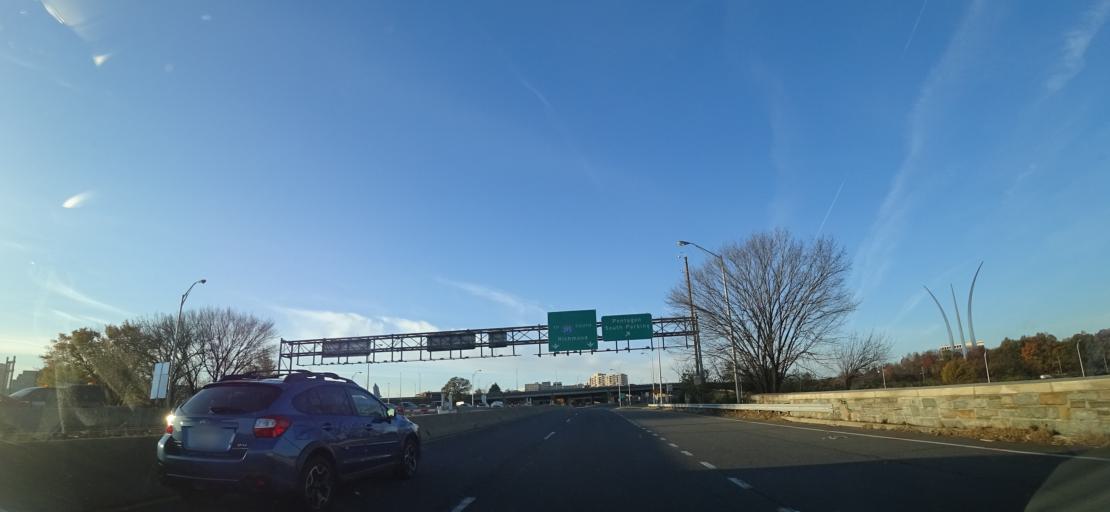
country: US
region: Washington, D.C.
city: Washington, D.C.
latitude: 38.8697
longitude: -77.0611
